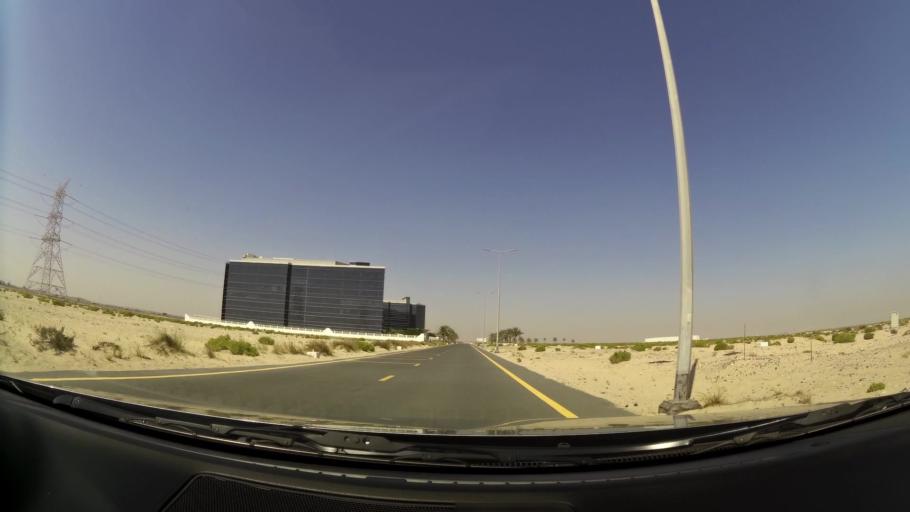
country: AE
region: Dubai
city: Dubai
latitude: 24.8995
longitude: 55.0631
